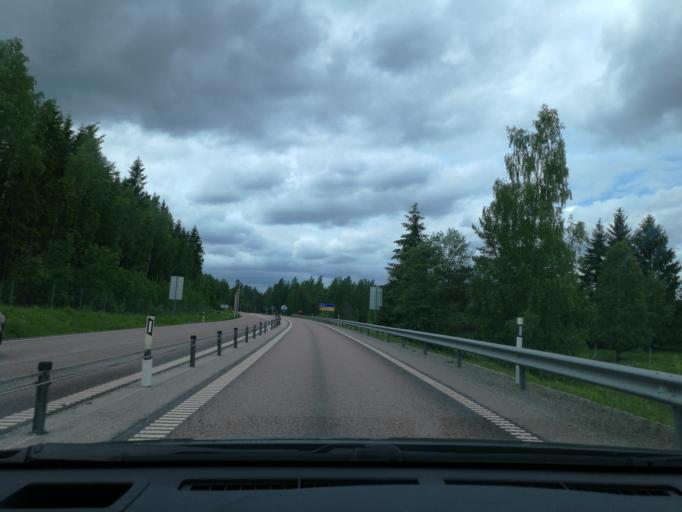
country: SE
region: Vaestmanland
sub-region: Fagersta Kommun
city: Fagersta
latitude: 59.9770
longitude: 15.8236
